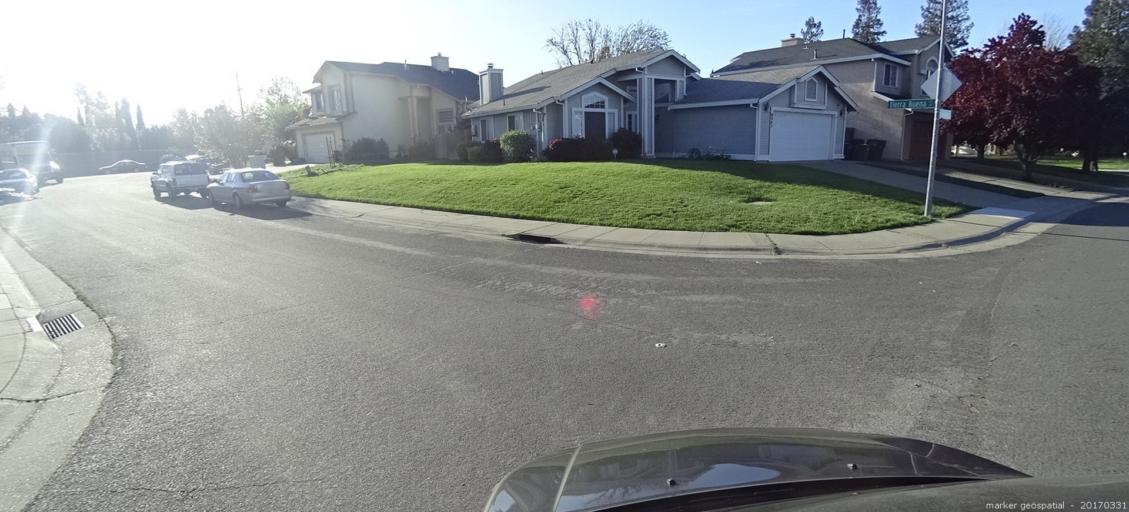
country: US
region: California
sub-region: Sacramento County
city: Parkway
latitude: 38.4650
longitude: -121.4479
